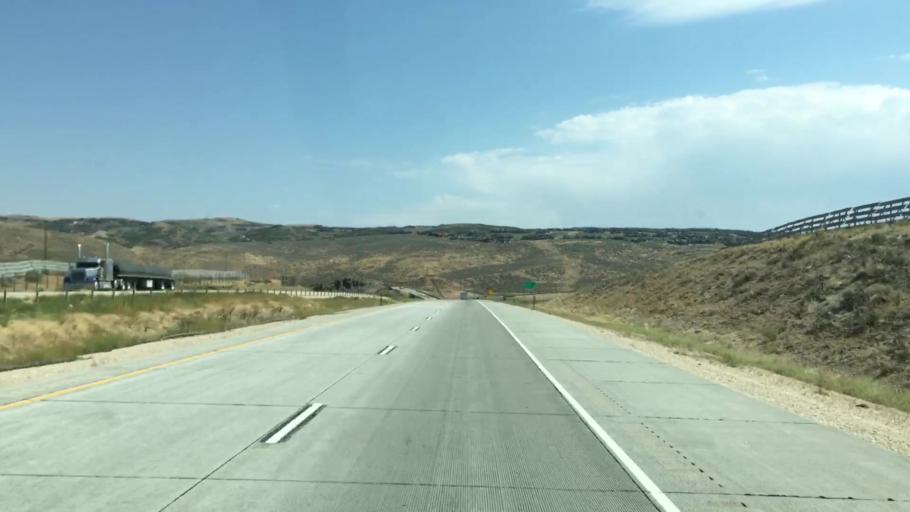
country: US
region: Utah
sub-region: Summit County
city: Snyderville
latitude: 40.7385
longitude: -111.4823
